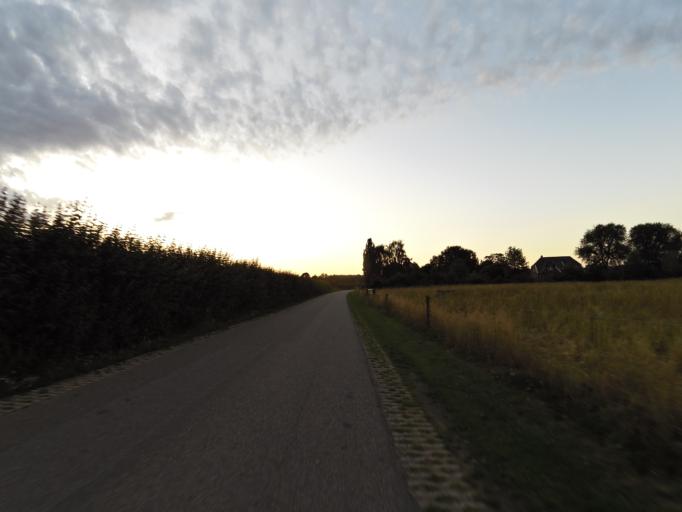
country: NL
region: Gelderland
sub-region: Oude IJsselstreek
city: Gendringen
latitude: 51.8455
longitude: 6.3965
